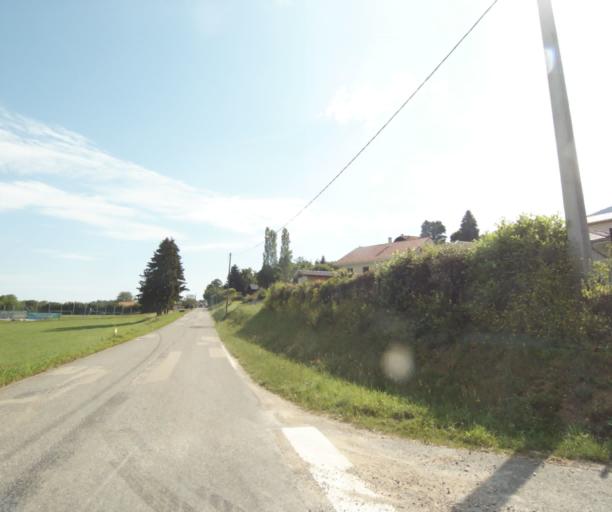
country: FR
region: Rhone-Alpes
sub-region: Departement de la Haute-Savoie
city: Lyaud
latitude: 46.3348
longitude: 6.5157
